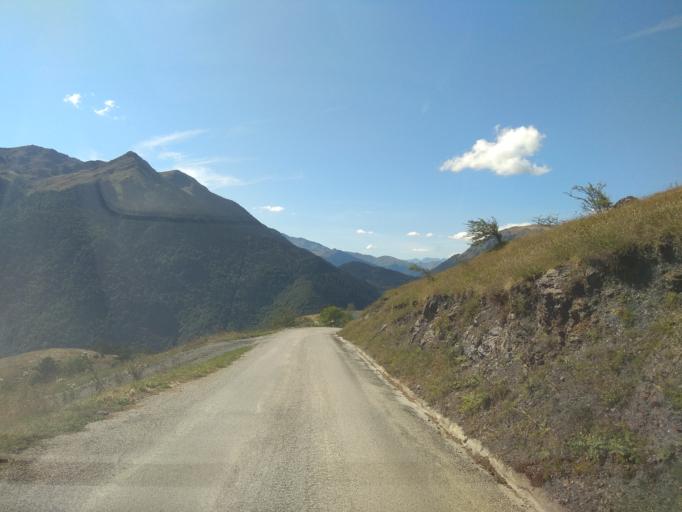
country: ES
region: Catalonia
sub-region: Provincia de Lleida
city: Les
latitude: 42.7588
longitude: 0.7104
